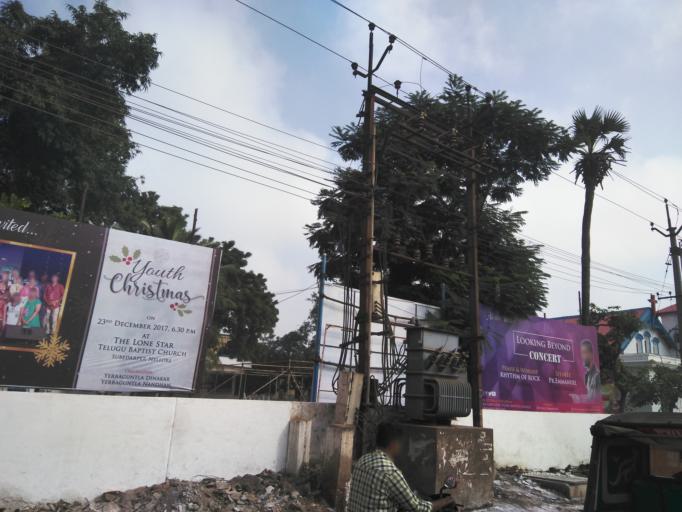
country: IN
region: Andhra Pradesh
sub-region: Nellore
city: Nellore
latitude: 14.4572
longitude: 79.9880
